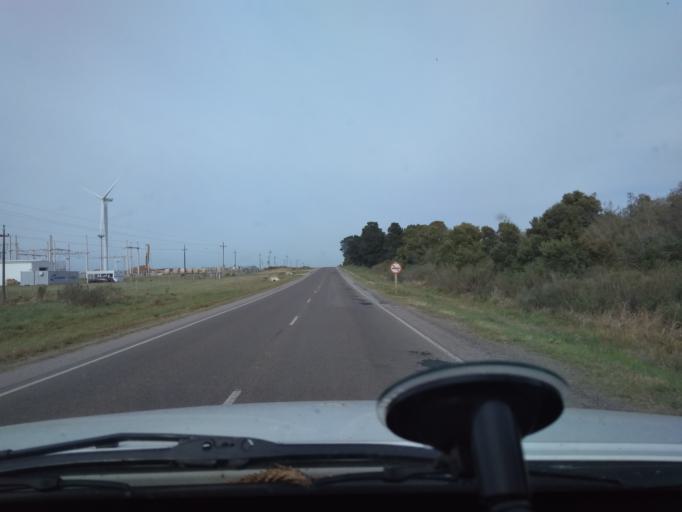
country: UY
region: Florida
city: Florida
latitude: -34.0938
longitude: -56.1021
